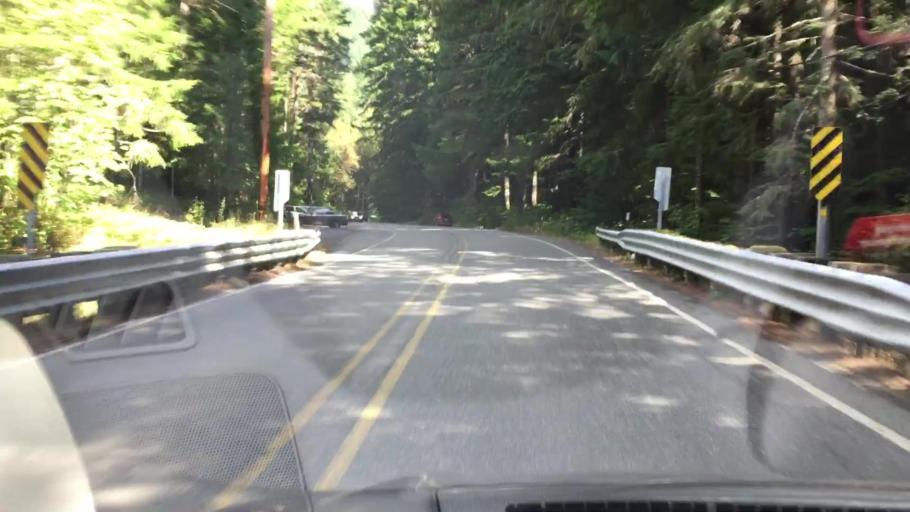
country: US
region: Washington
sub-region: Pierce County
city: Eatonville
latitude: 46.7552
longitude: -121.9616
